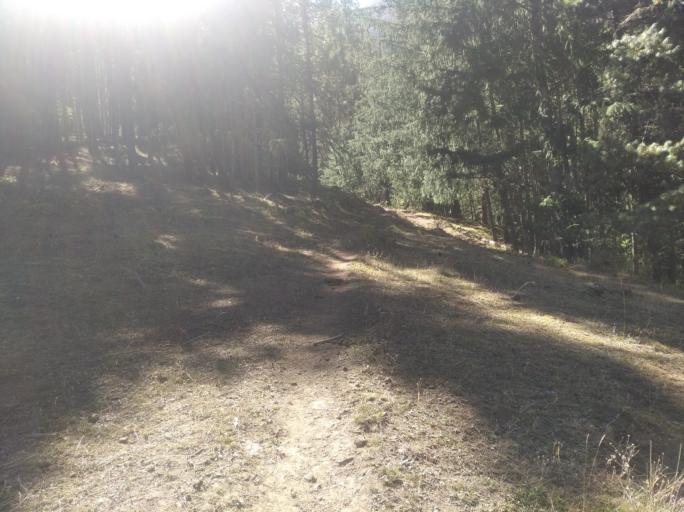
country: NP
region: Western Region
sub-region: Dhawalagiri Zone
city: Jomsom
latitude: 28.8858
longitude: 83.0673
